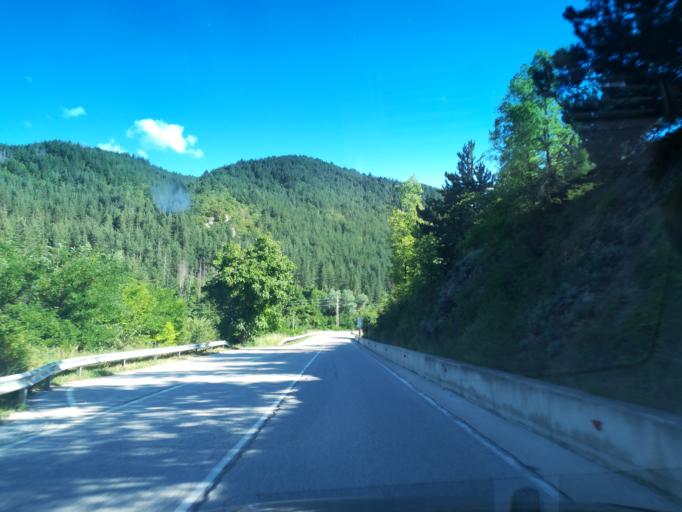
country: BG
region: Smolyan
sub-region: Obshtina Chepelare
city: Chepelare
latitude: 41.8531
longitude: 24.6841
